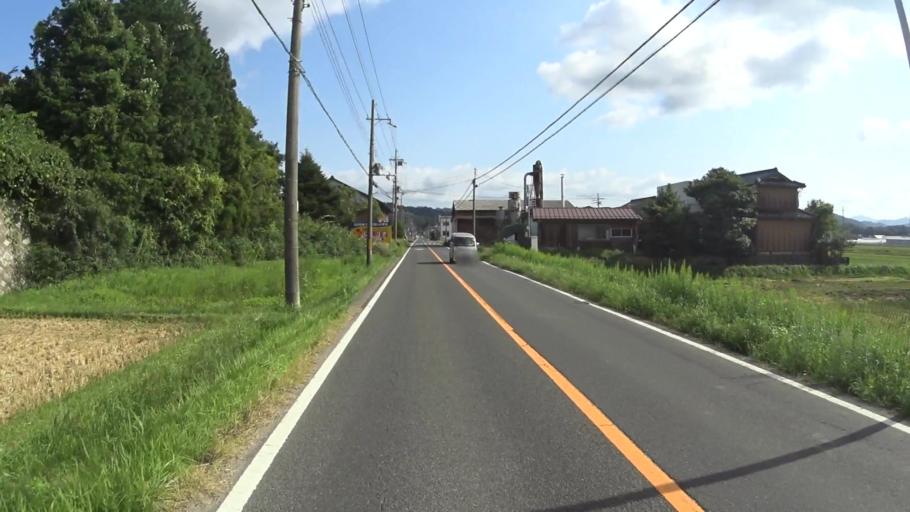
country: JP
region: Kyoto
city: Miyazu
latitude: 35.5955
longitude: 135.0965
